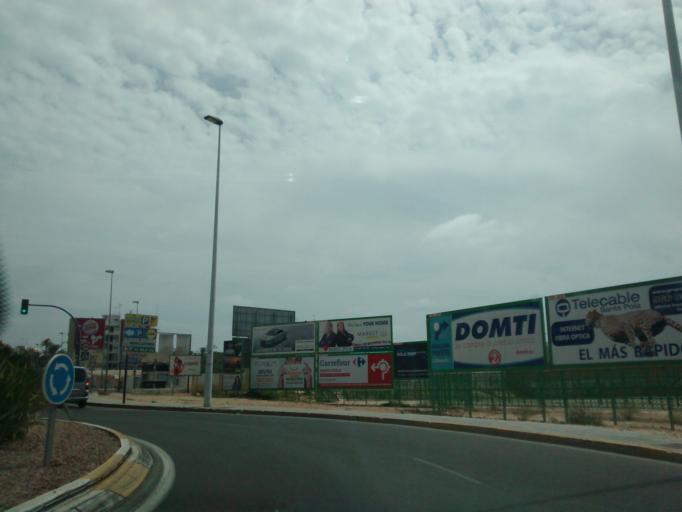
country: ES
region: Valencia
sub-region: Provincia de Alicante
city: Santa Pola
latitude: 38.1969
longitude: -0.5628
